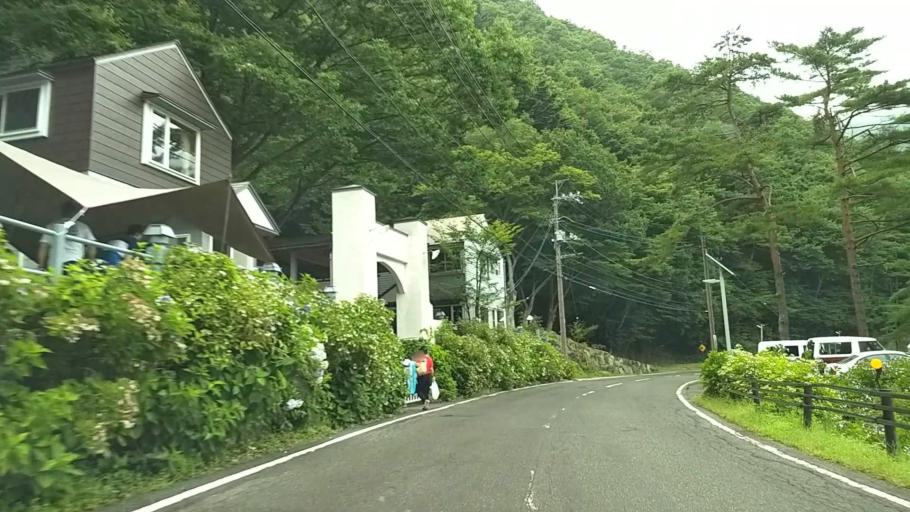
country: JP
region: Yamanashi
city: Fujikawaguchiko
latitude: 35.4890
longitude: 138.6028
